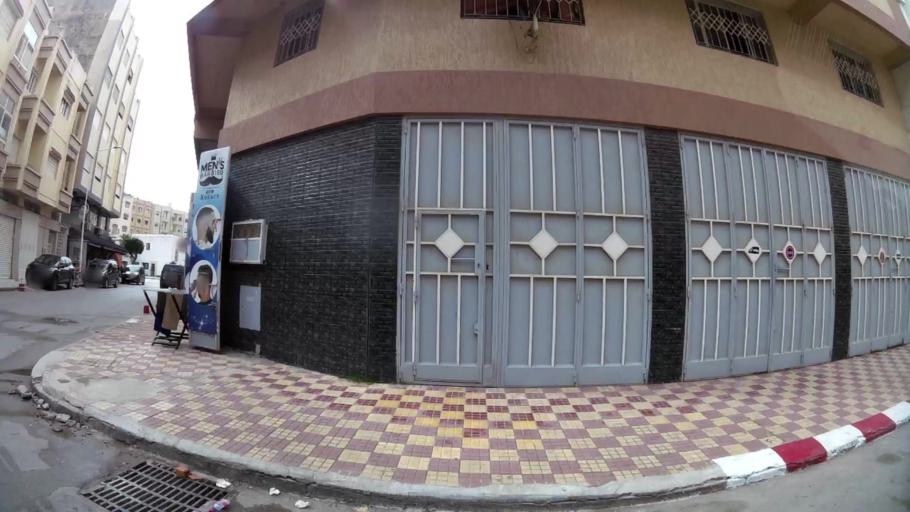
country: MA
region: Tanger-Tetouan
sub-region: Tanger-Assilah
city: Tangier
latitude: 35.7536
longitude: -5.7990
